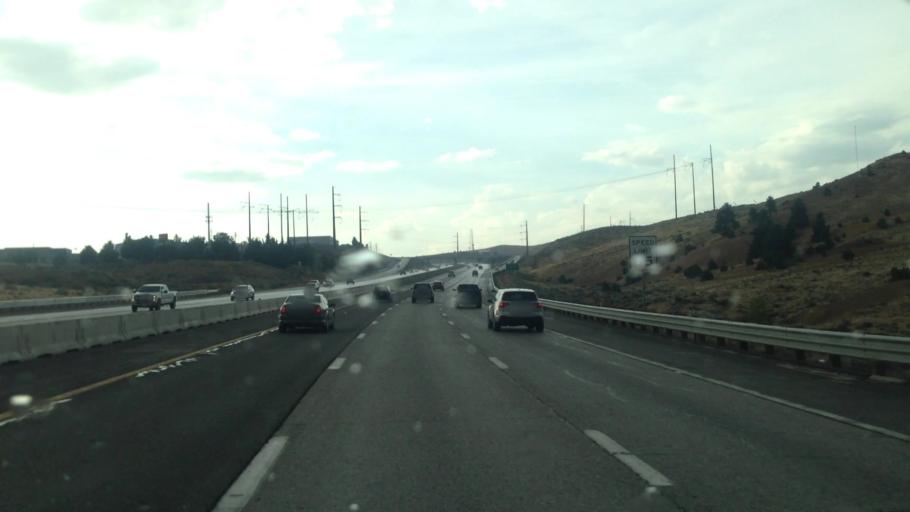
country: US
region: Nevada
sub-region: Washoe County
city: Reno
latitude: 39.5664
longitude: -119.8031
